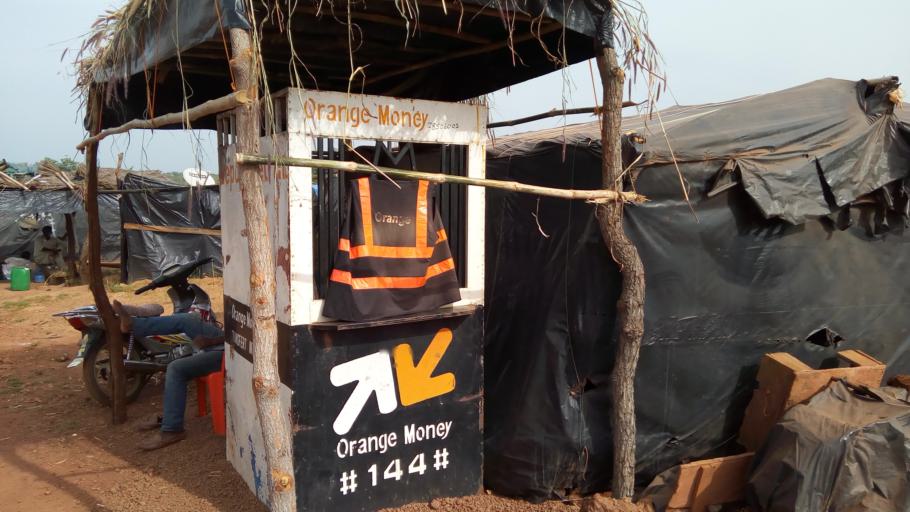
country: ML
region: Koulikoro
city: Kangaba
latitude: 11.6021
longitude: -8.6021
